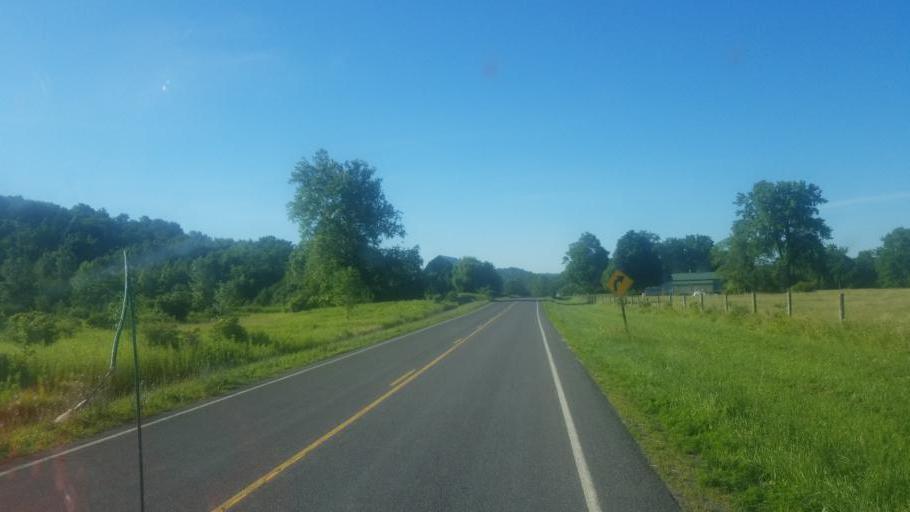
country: US
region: New York
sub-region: Wayne County
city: Lyons
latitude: 43.0925
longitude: -77.0413
